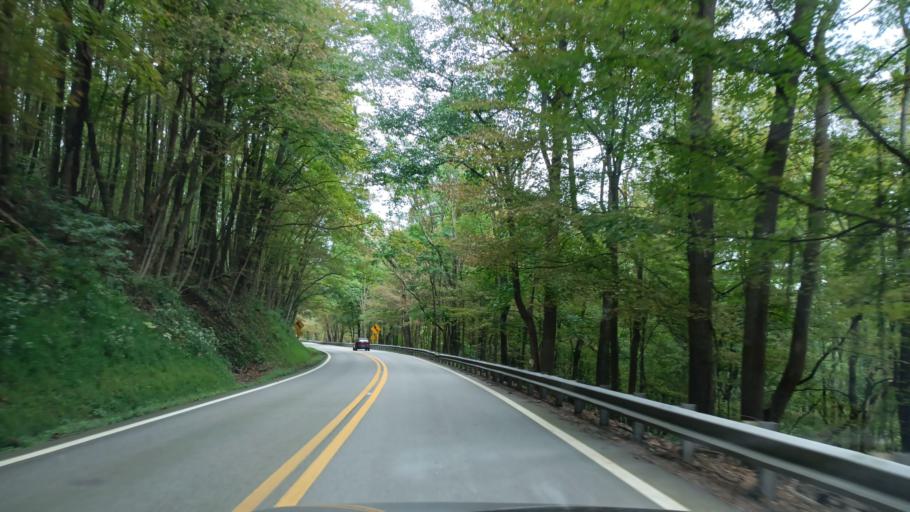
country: US
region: West Virginia
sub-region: Taylor County
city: Grafton
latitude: 39.3305
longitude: -79.9267
